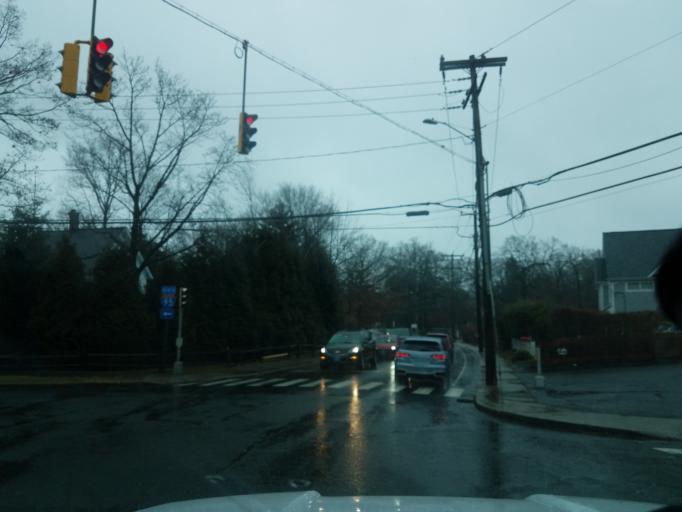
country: US
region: Connecticut
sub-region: Fairfield County
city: Darien
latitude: 41.0674
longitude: -73.4900
